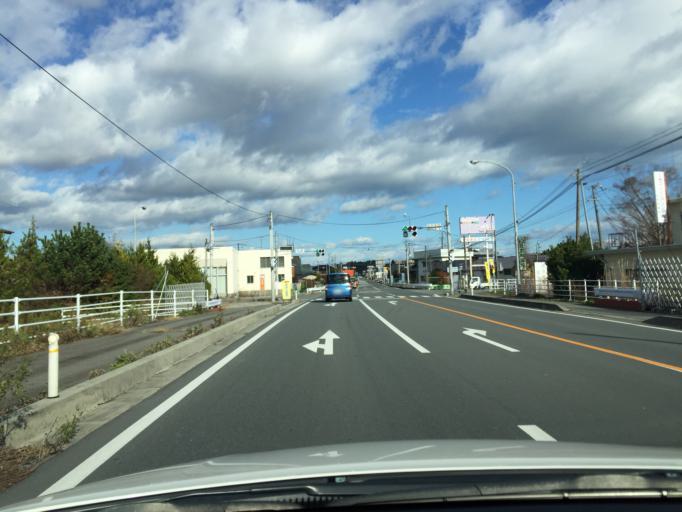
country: JP
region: Fukushima
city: Namie
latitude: 37.4468
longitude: 141.0085
